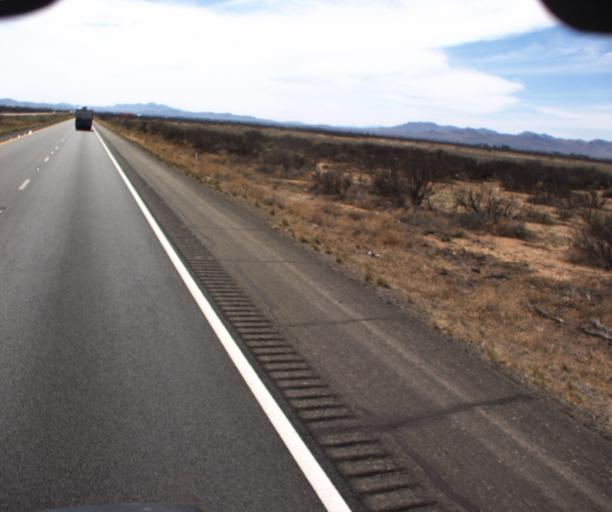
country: US
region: Arizona
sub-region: Cochise County
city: Willcox
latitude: 32.2965
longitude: -109.8108
